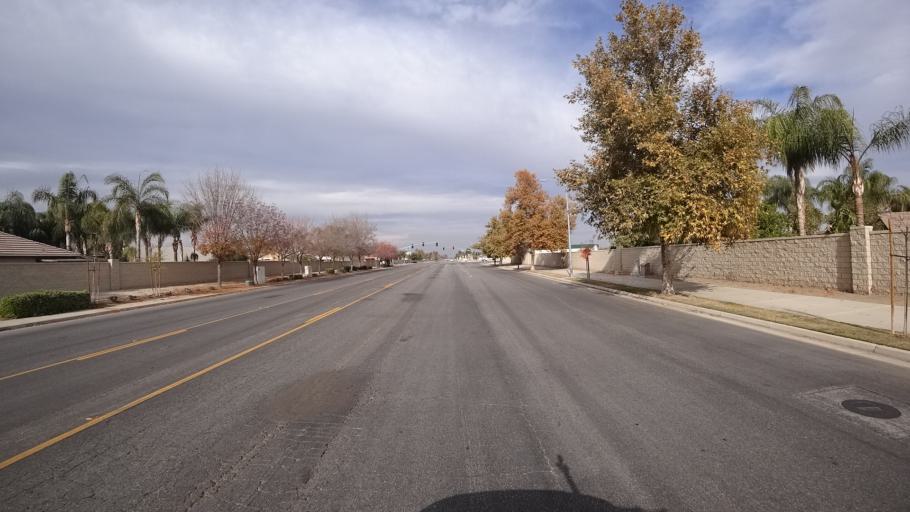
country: US
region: California
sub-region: Kern County
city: Rosedale
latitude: 35.4183
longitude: -119.1366
